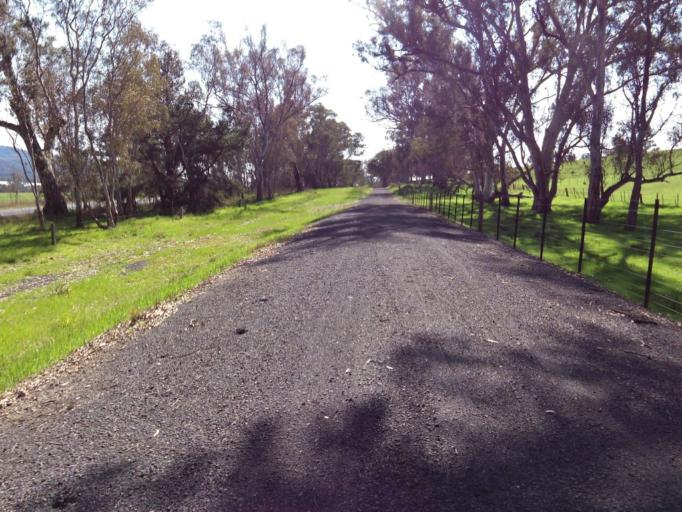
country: AU
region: Victoria
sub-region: Murrindindi
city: Alexandra
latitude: -37.1381
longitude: 145.5910
